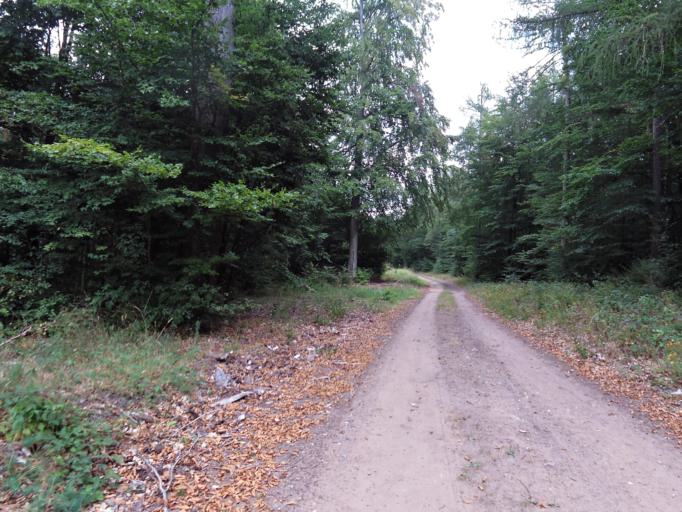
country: DE
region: Rheinland-Pfalz
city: Elmstein
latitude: 49.3816
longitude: 7.9371
